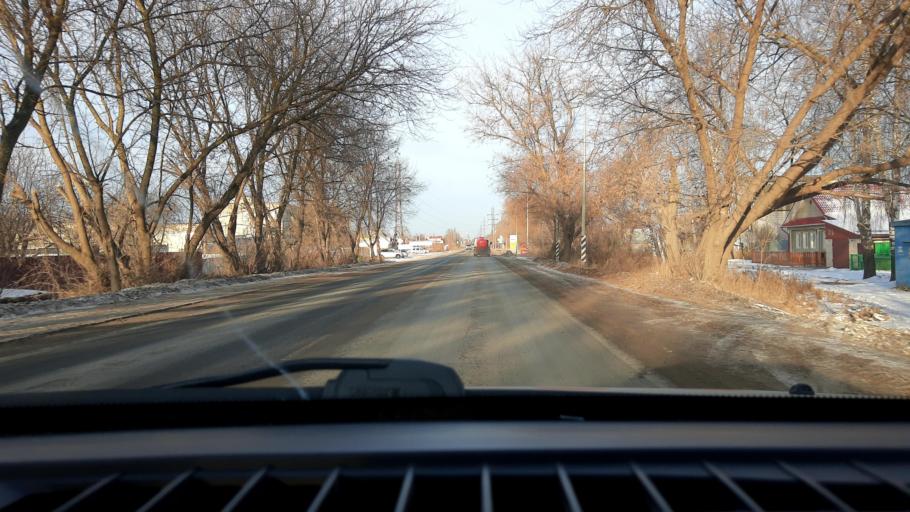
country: RU
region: Nizjnij Novgorod
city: Bor
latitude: 56.3681
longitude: 44.0688
